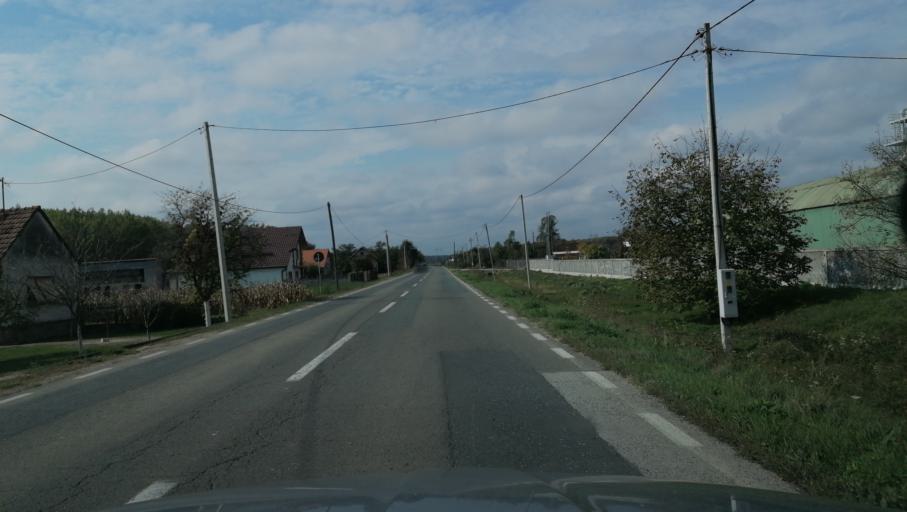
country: RS
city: Bosut
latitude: 44.9246
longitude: 19.3384
